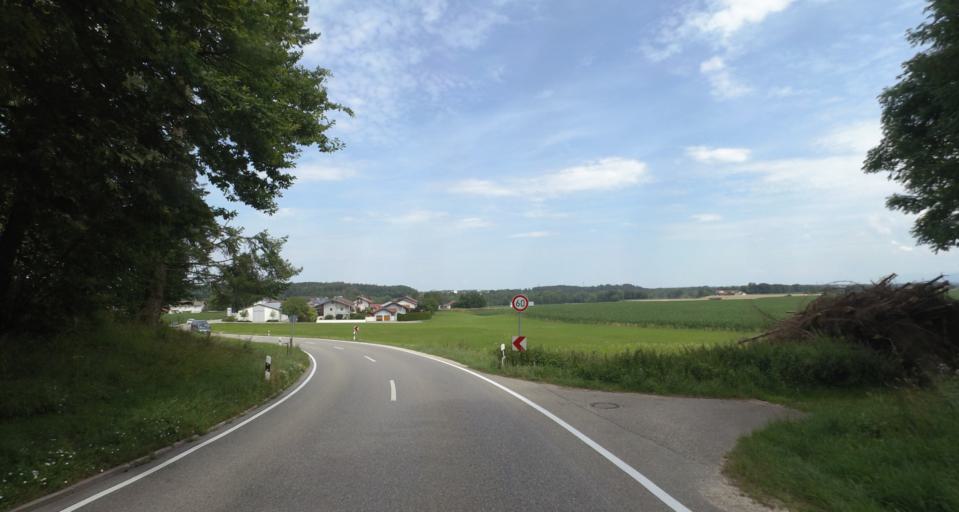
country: DE
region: Bavaria
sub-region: Upper Bavaria
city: Traunreut
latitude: 47.9560
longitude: 12.5640
